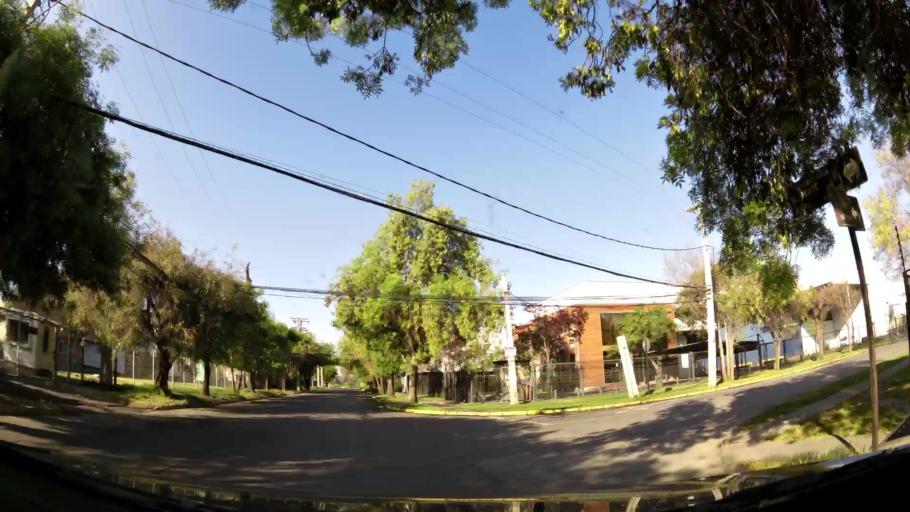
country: CL
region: Santiago Metropolitan
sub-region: Provincia de Santiago
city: Santiago
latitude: -33.3727
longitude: -70.6519
